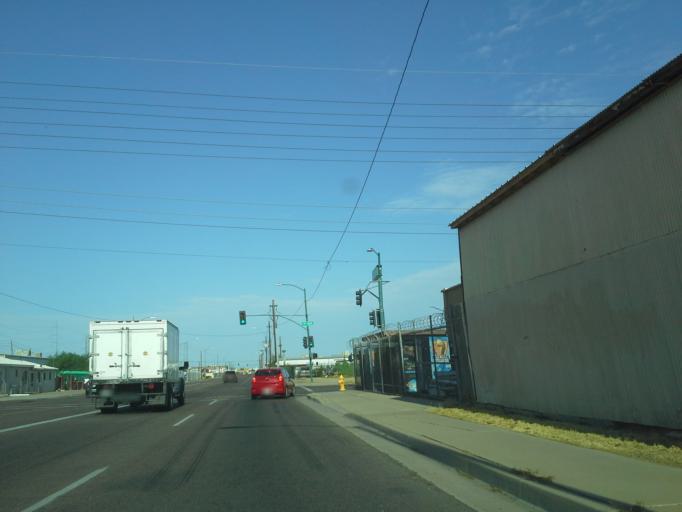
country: US
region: Arizona
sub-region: Maricopa County
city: Phoenix
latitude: 33.4415
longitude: -112.0952
